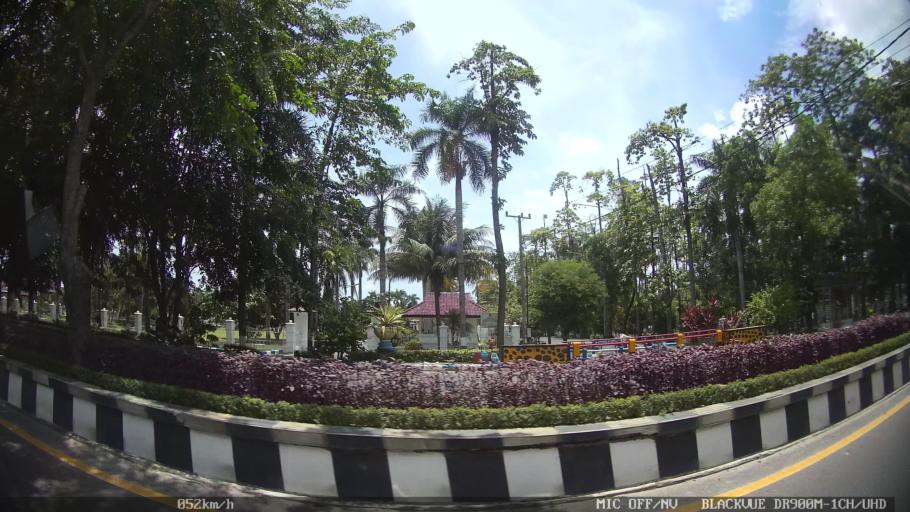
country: ID
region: North Sumatra
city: Percut
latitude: 3.5517
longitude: 98.8672
